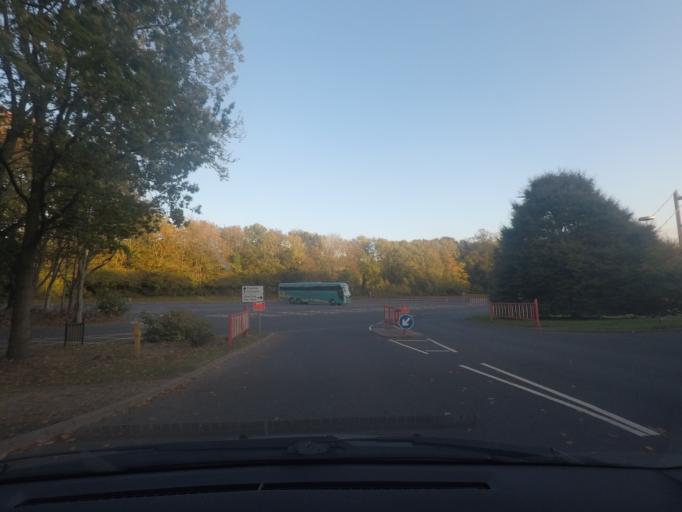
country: GB
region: England
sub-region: East Riding of Yorkshire
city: Hessle
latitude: 53.7202
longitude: -0.4536
